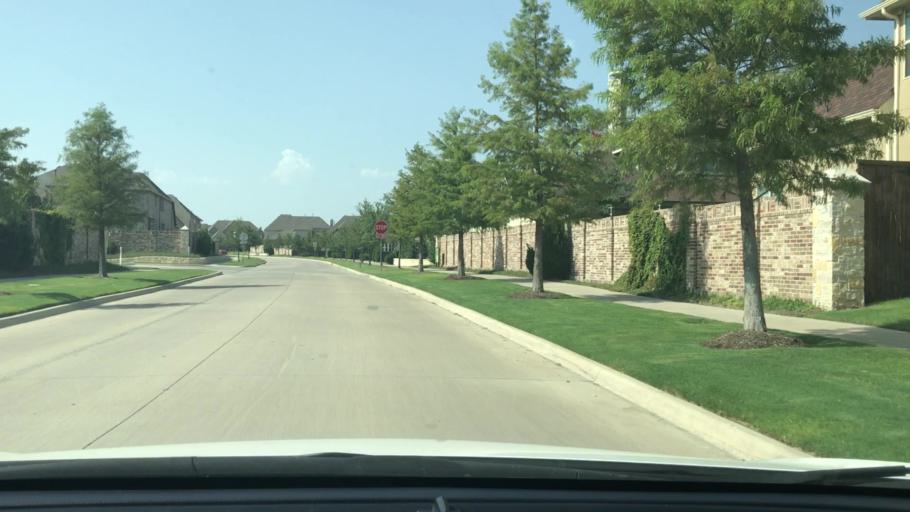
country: US
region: Texas
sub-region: Collin County
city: Frisco
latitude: 33.1300
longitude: -96.7644
